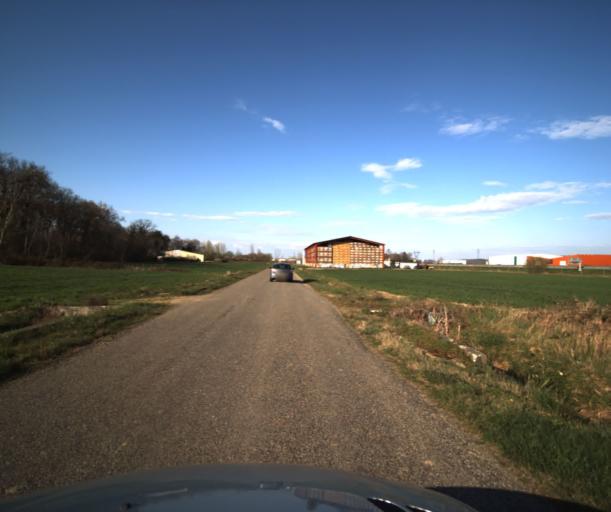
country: FR
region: Midi-Pyrenees
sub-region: Departement du Tarn-et-Garonne
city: Bressols
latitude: 43.9469
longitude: 1.3228
